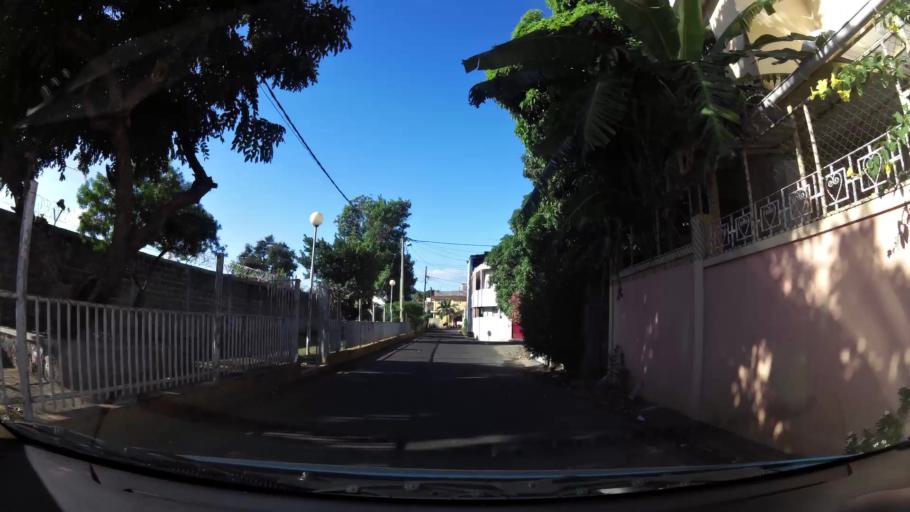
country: MU
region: Port Louis
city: Port Louis
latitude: -20.1674
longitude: 57.4798
